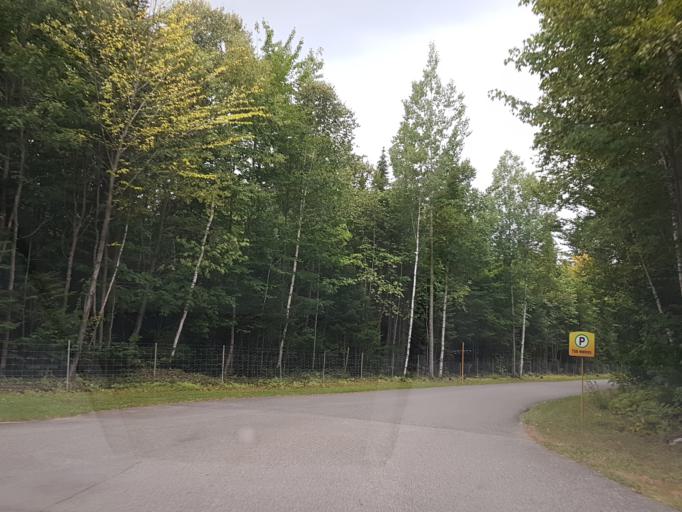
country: CA
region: Quebec
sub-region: Capitale-Nationale
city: Beaupre
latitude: 47.0647
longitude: -70.8673
